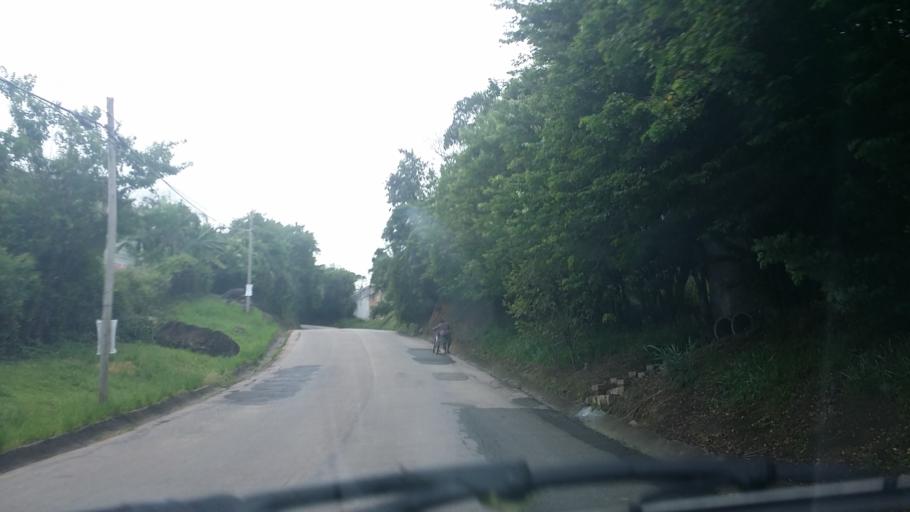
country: BR
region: Sao Paulo
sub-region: Itupeva
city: Itupeva
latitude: -23.1713
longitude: -47.1092
